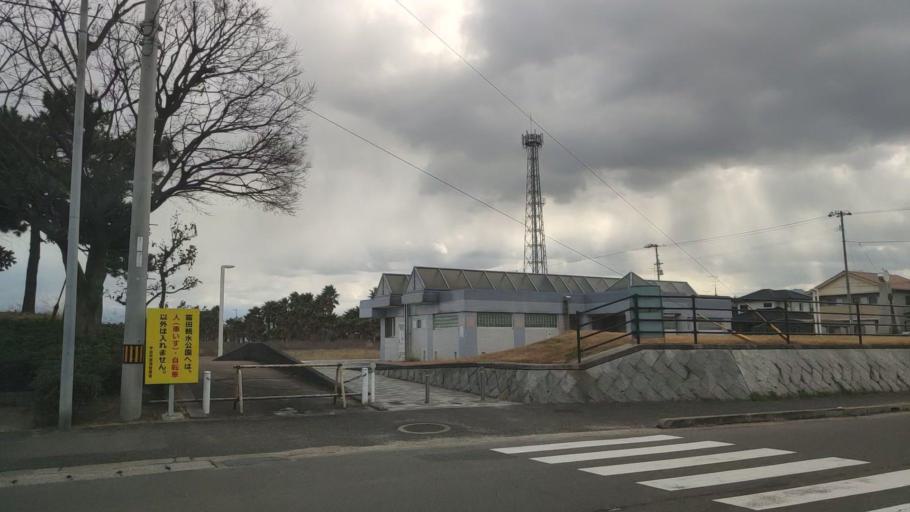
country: JP
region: Ehime
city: Saijo
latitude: 34.0461
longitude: 133.0291
